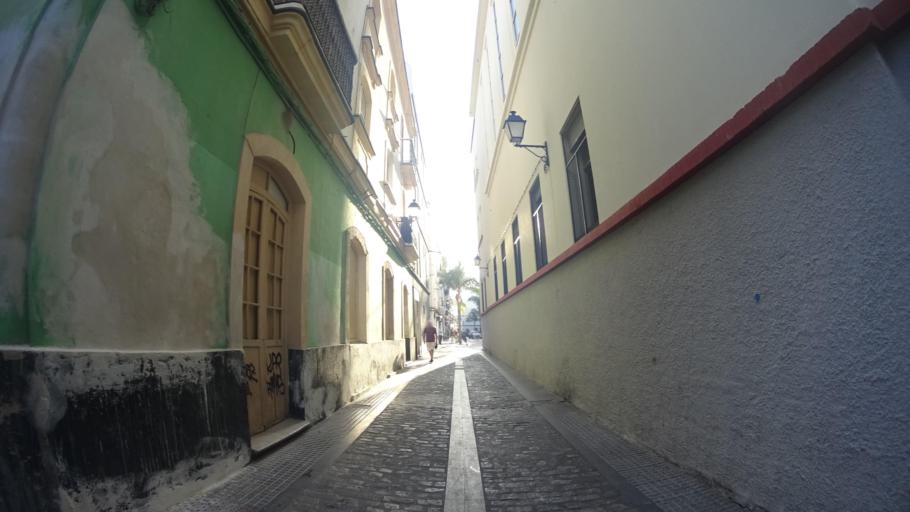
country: ES
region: Andalusia
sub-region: Provincia de Cadiz
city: Cadiz
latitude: 36.5301
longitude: -6.3022
